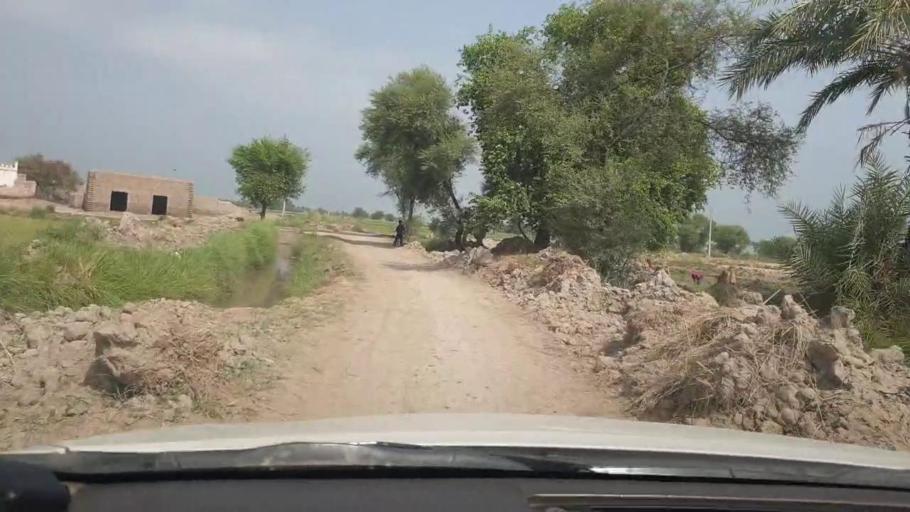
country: PK
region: Sindh
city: Shikarpur
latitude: 28.0158
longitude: 68.5942
